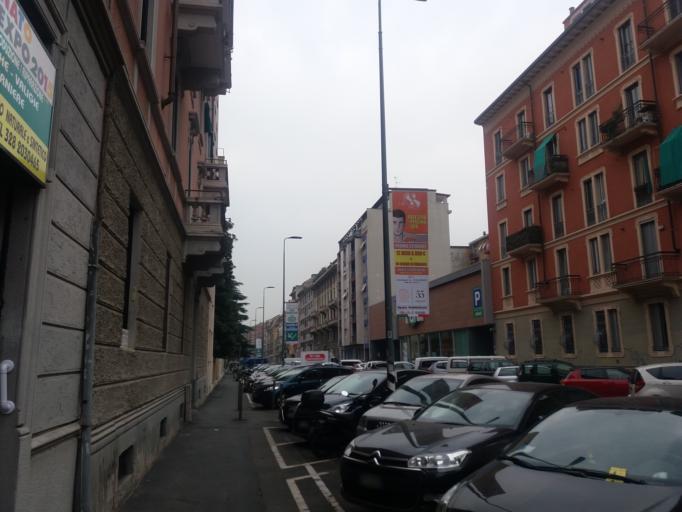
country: IT
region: Lombardy
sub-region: Citta metropolitana di Milano
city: Milano
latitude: 45.4841
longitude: 9.2252
